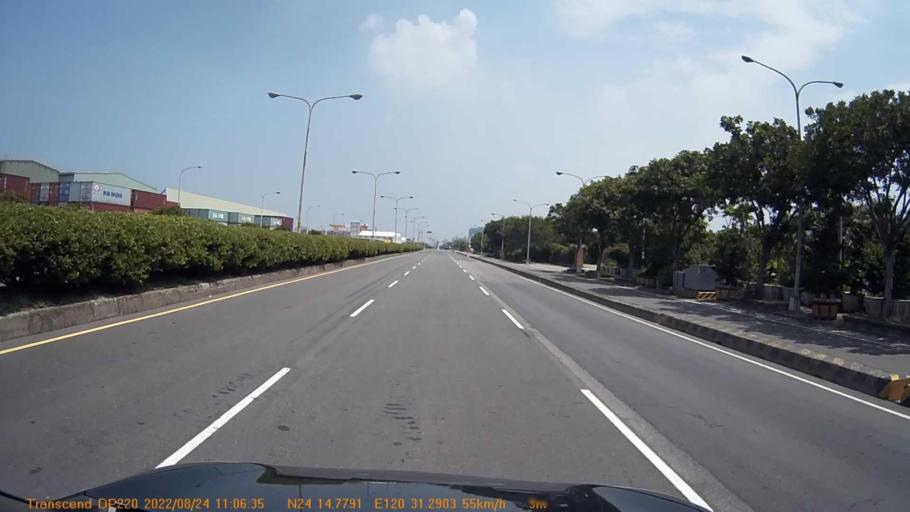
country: TW
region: Taiwan
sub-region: Changhua
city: Chang-hua
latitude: 24.2467
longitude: 120.5217
